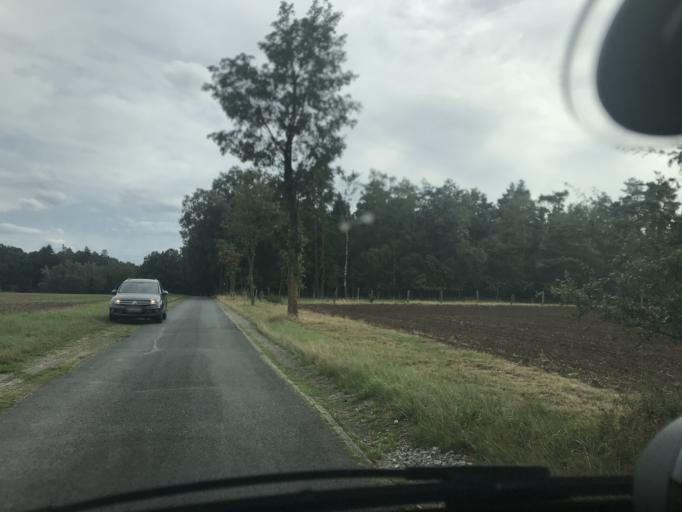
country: DE
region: Lower Saxony
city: Hollenstedt
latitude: 53.3895
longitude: 9.7257
